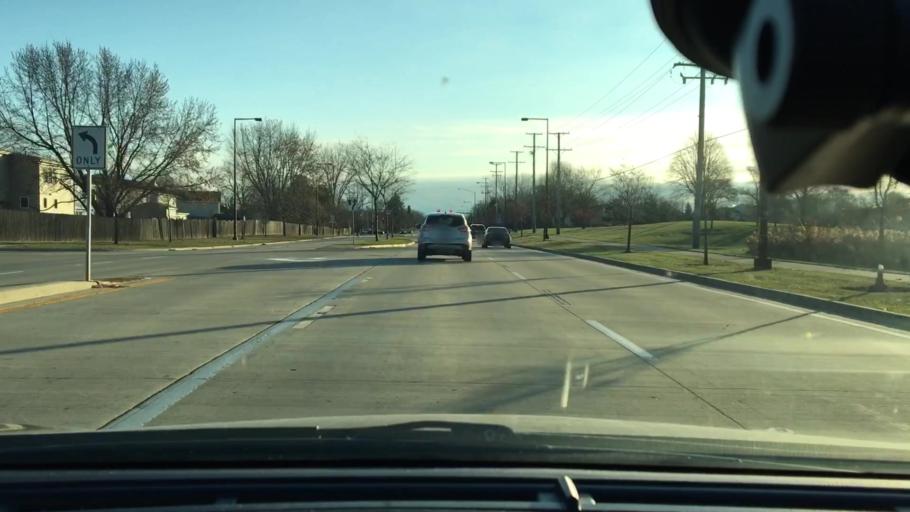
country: US
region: Illinois
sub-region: Cook County
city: Buffalo Grove
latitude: 42.1717
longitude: -87.9683
